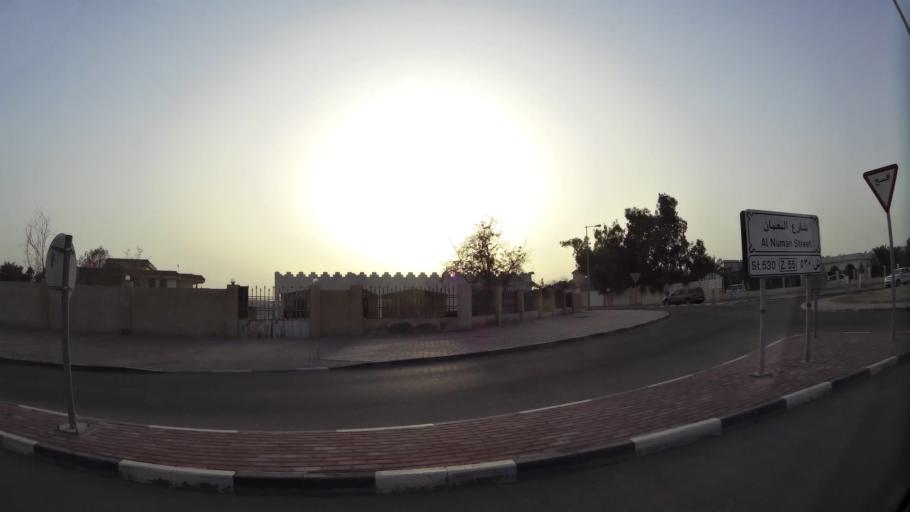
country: QA
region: Baladiyat ar Rayyan
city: Ar Rayyan
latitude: 25.2409
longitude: 51.4449
